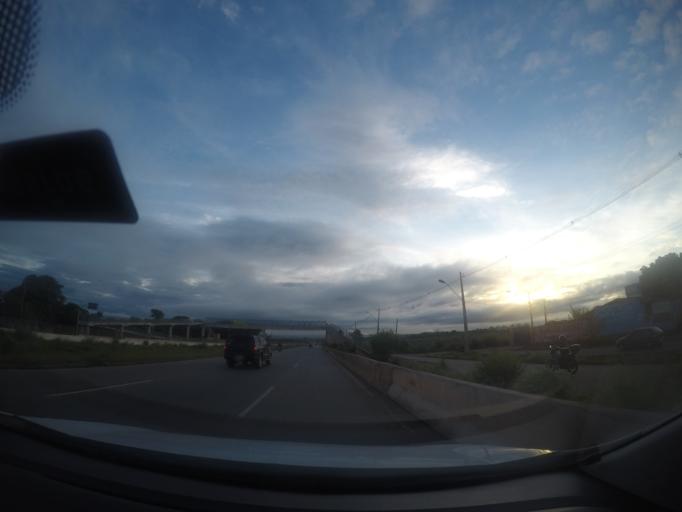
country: BR
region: Goias
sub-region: Goiania
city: Goiania
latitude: -16.7145
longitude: -49.3605
